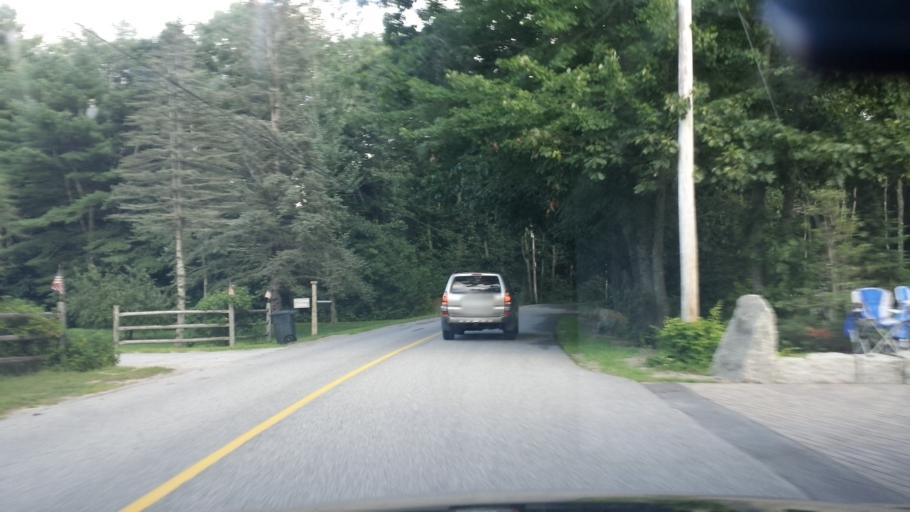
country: US
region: Maine
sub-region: York County
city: Arundel
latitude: 43.4281
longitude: -70.4516
